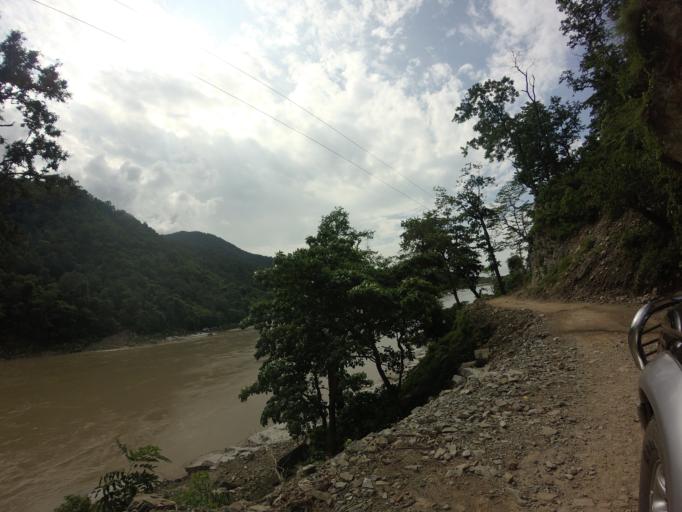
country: NP
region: Far Western
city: Tikapur
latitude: 28.6507
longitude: 81.2870
